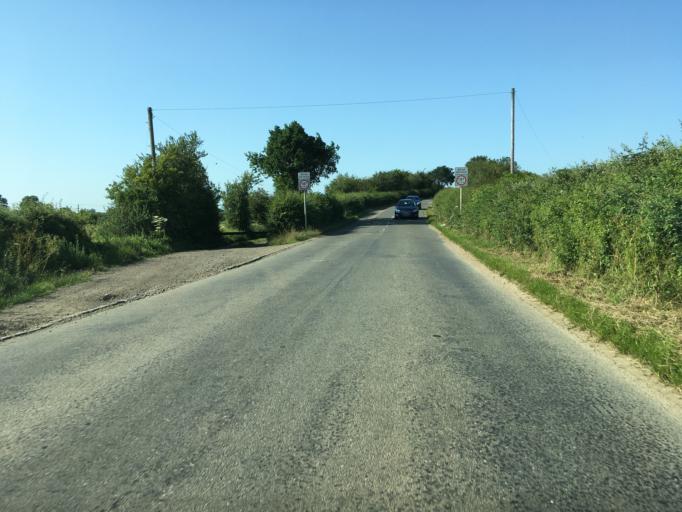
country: GB
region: England
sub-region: Buckinghamshire
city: Steeple Claydon
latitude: 51.9291
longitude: -1.0223
